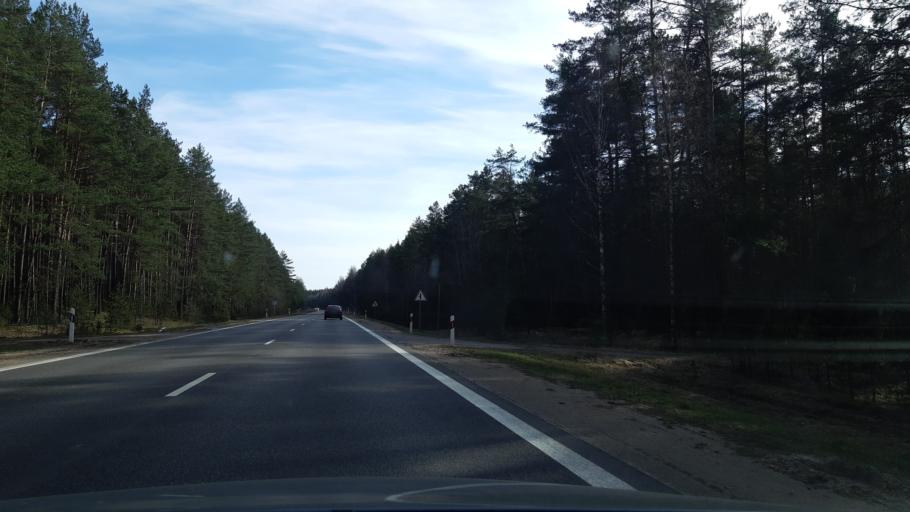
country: LT
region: Alytaus apskritis
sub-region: Alytaus rajonas
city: Daugai
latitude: 54.1638
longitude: 24.2085
